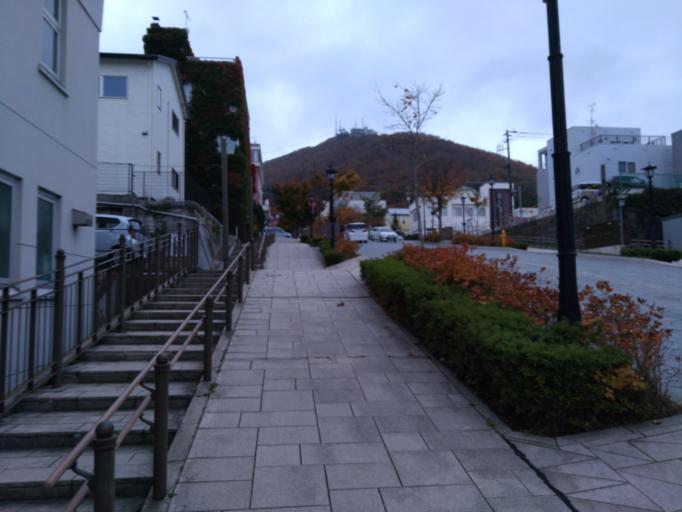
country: JP
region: Hokkaido
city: Hakodate
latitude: 41.7655
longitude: 140.7137
